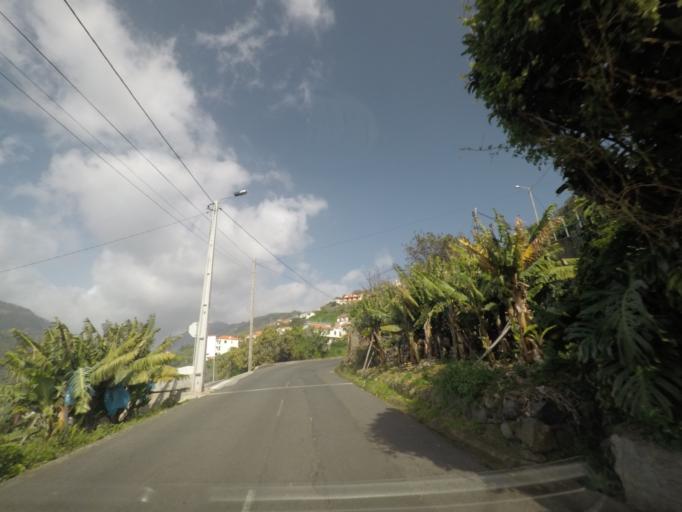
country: PT
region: Madeira
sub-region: Ribeira Brava
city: Campanario
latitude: 32.6746
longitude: -17.0584
